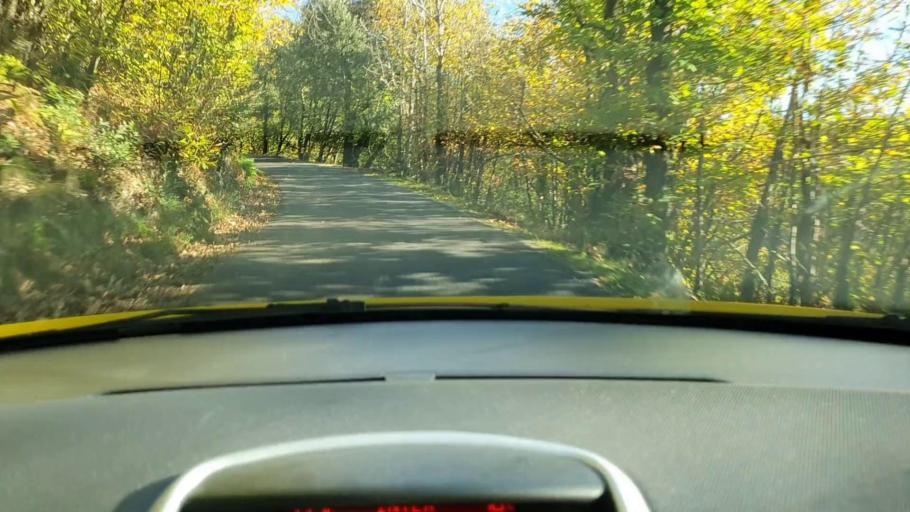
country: FR
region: Languedoc-Roussillon
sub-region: Departement du Gard
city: Sumene
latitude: 44.0152
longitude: 3.7763
